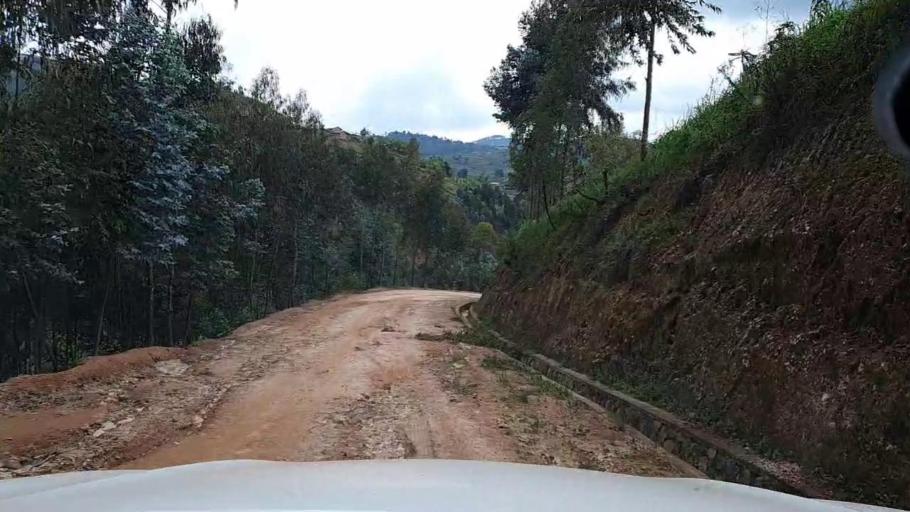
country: RW
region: Southern Province
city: Nzega
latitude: -2.6950
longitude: 29.4427
